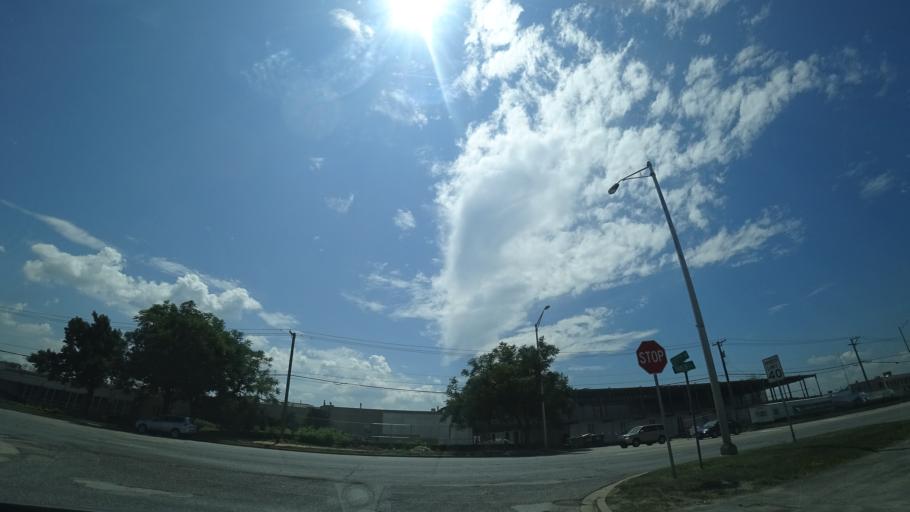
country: US
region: Illinois
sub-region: Cook County
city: Robbins
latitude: 41.6624
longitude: -87.7142
